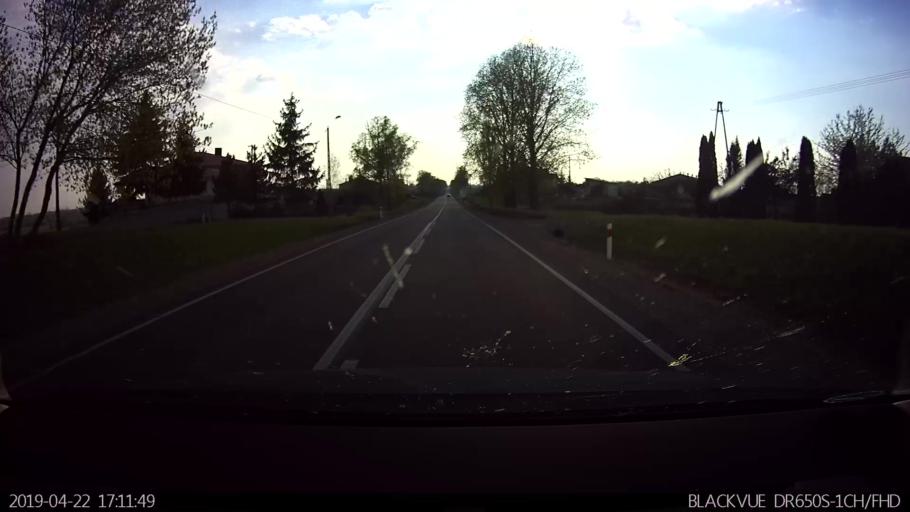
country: PL
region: Masovian Voivodeship
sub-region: Powiat siedlecki
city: Korczew
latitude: 52.4110
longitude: 22.5466
